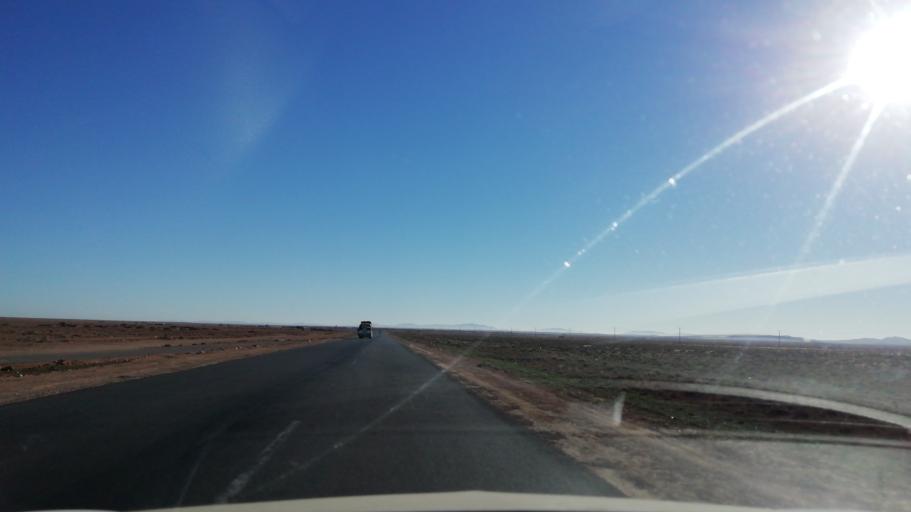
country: DZ
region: El Bayadh
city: El Bayadh
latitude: 33.8570
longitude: 0.5848
